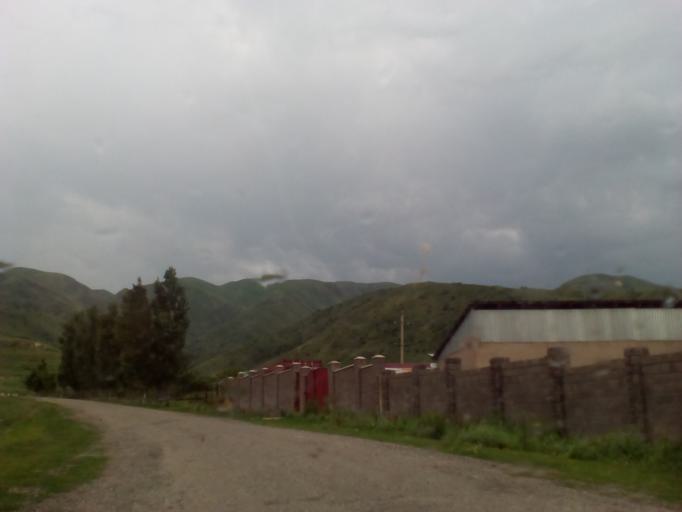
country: KZ
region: Almaty Oblysy
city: Burunday
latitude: 43.1516
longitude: 76.3852
